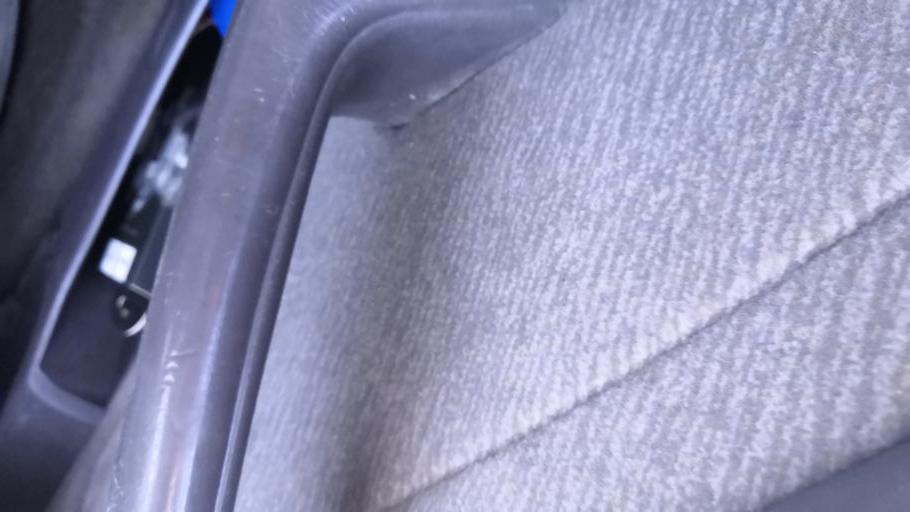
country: RU
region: Primorskiy
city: Lazo
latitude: 45.8244
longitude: 133.6131
